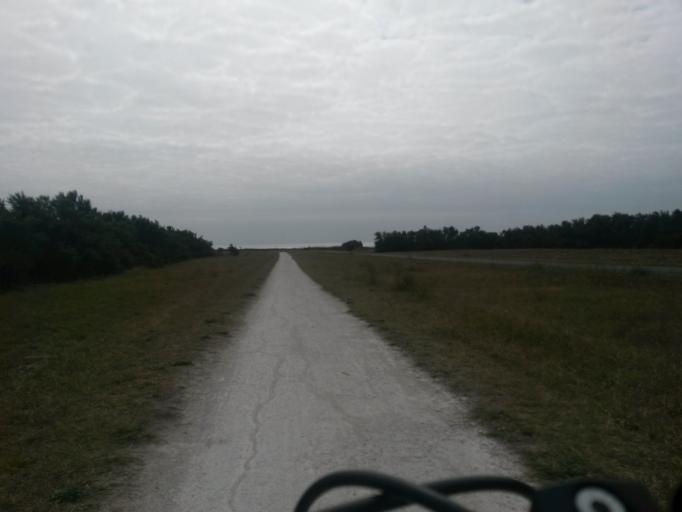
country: FR
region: Poitou-Charentes
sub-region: Departement de la Charente-Maritime
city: Saint-Denis-d'Oleron
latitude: 46.0436
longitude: -1.4082
